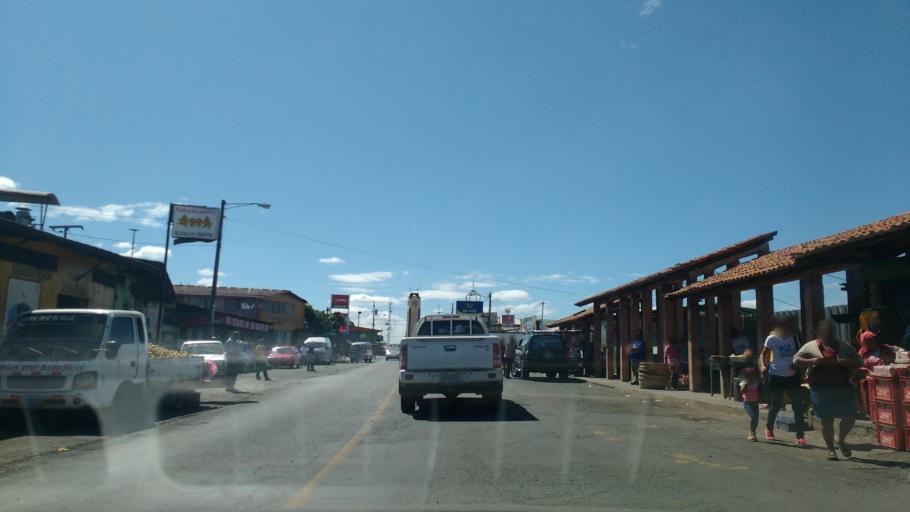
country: NI
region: Carazo
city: Diriamba
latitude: 11.8596
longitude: -86.2356
